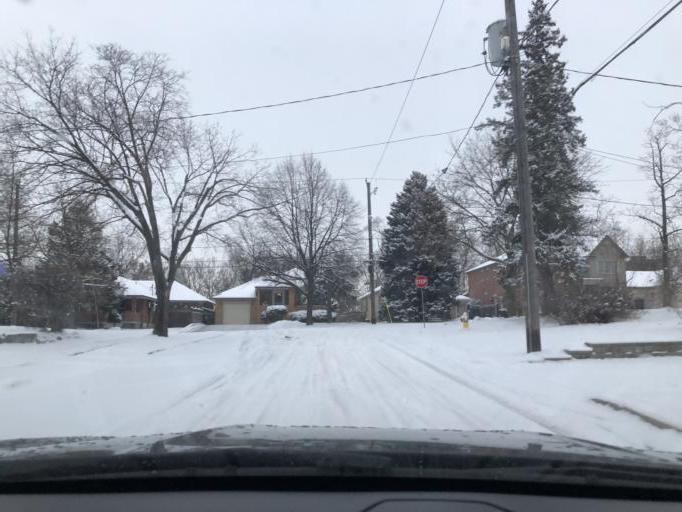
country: CA
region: Ontario
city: Toronto
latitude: 43.7019
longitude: -79.4826
